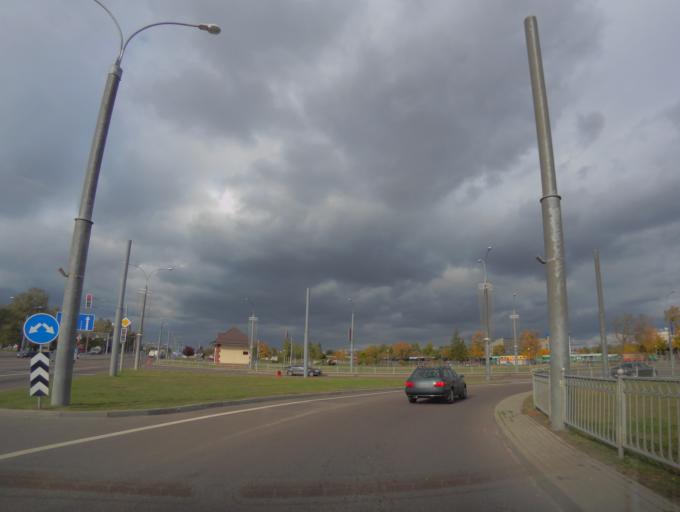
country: BY
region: Brest
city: Brest
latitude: 52.0850
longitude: 23.6698
